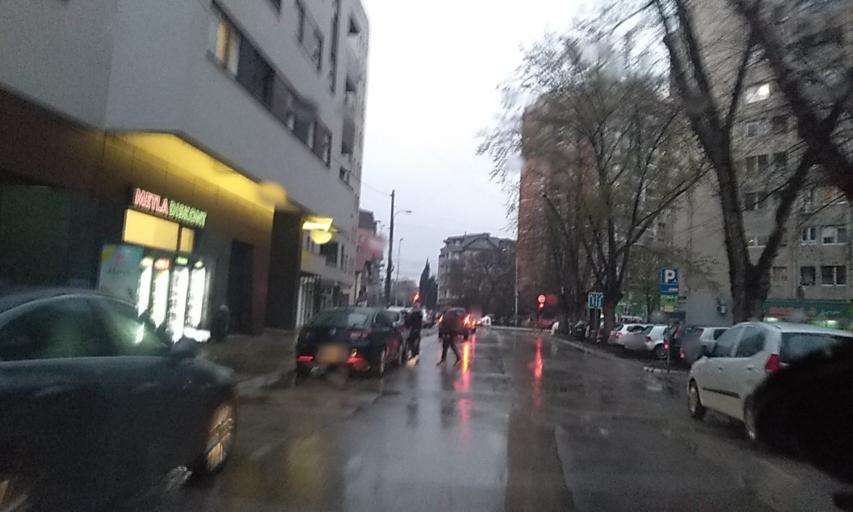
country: RS
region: Central Serbia
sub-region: Nisavski Okrug
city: Nis
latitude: 43.3241
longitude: 21.9062
